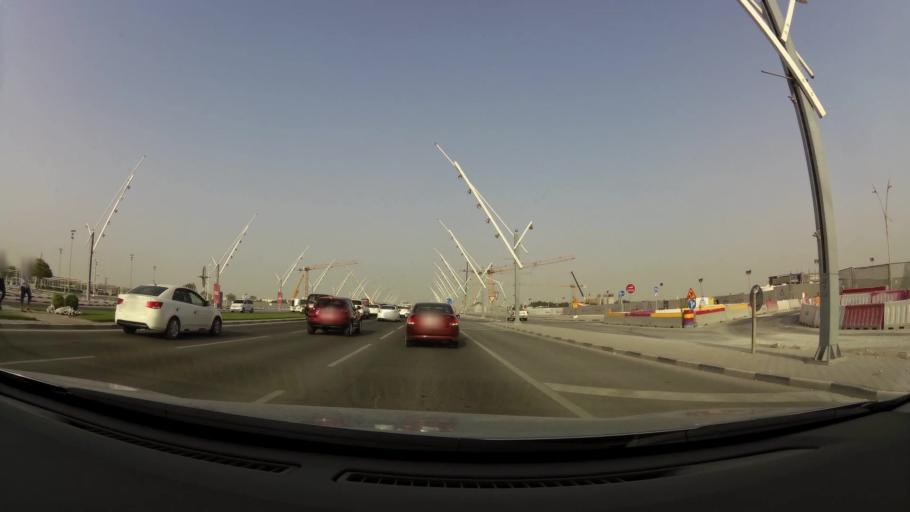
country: QA
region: Baladiyat ar Rayyan
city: Ar Rayyan
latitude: 25.2593
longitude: 51.4503
